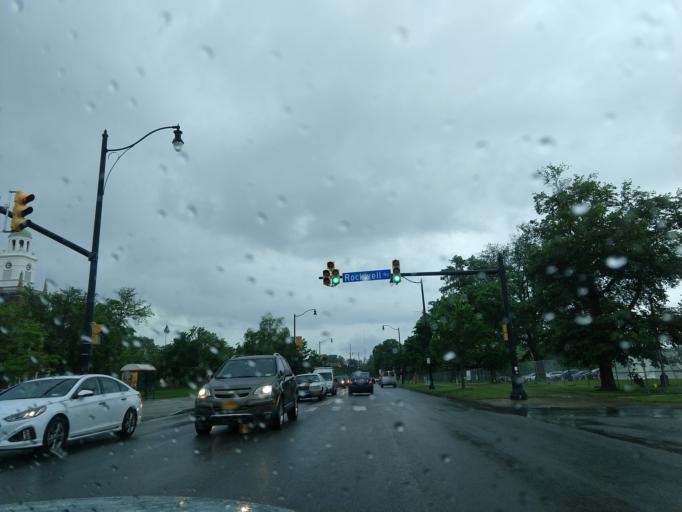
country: US
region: New York
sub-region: Erie County
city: Kenmore
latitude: 42.9318
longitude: -78.8770
